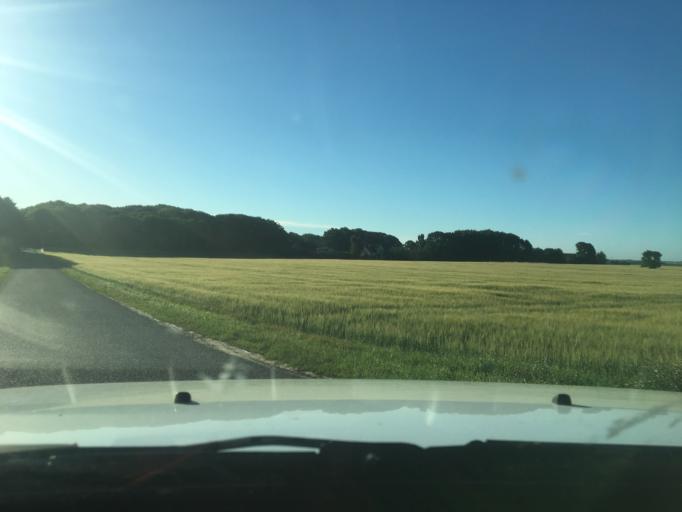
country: DK
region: Central Jutland
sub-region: Randers Kommune
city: Randers
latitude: 56.4010
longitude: 10.0642
